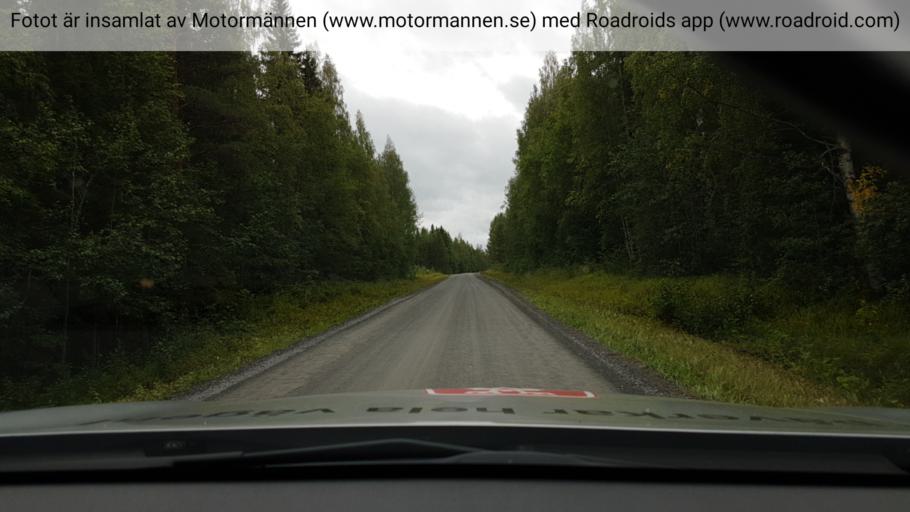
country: SE
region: Vaesterbotten
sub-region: Skelleftea Kommun
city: Forsbacka
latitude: 64.8336
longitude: 20.5023
